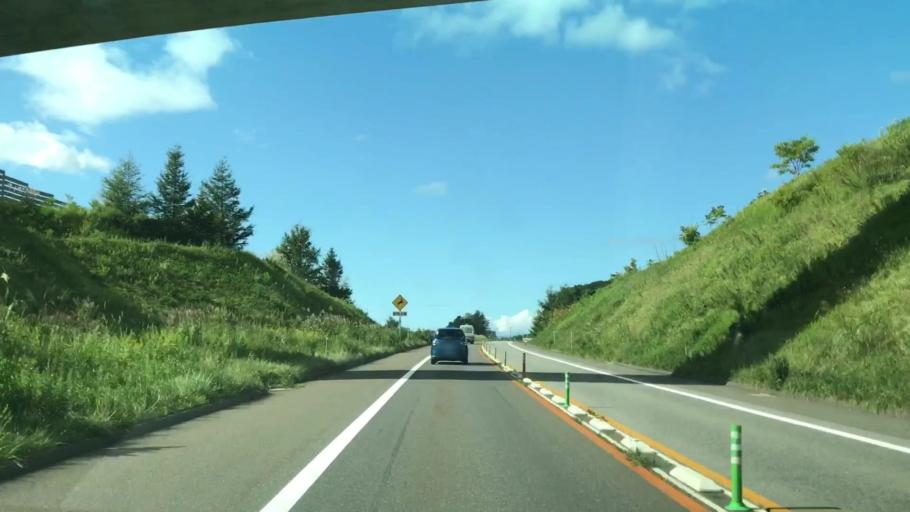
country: JP
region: Hokkaido
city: Date
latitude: 42.4461
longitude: 140.9143
